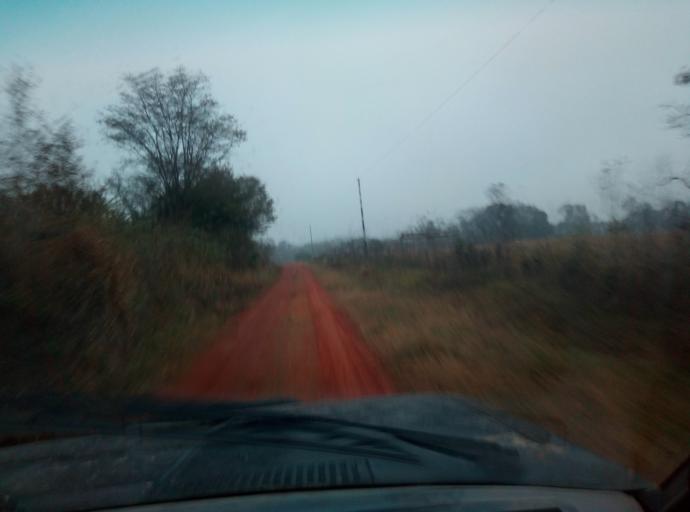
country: PY
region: Caaguazu
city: Doctor Cecilio Baez
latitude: -25.1592
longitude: -56.2597
